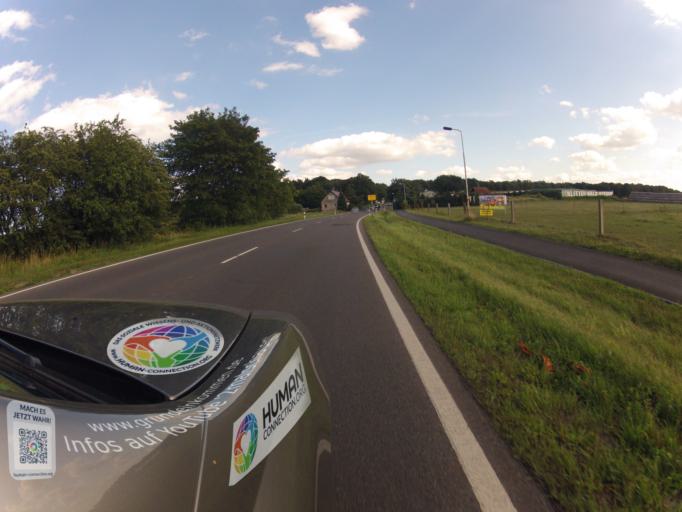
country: DE
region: Mecklenburg-Vorpommern
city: Loddin
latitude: 54.0310
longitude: 14.0294
